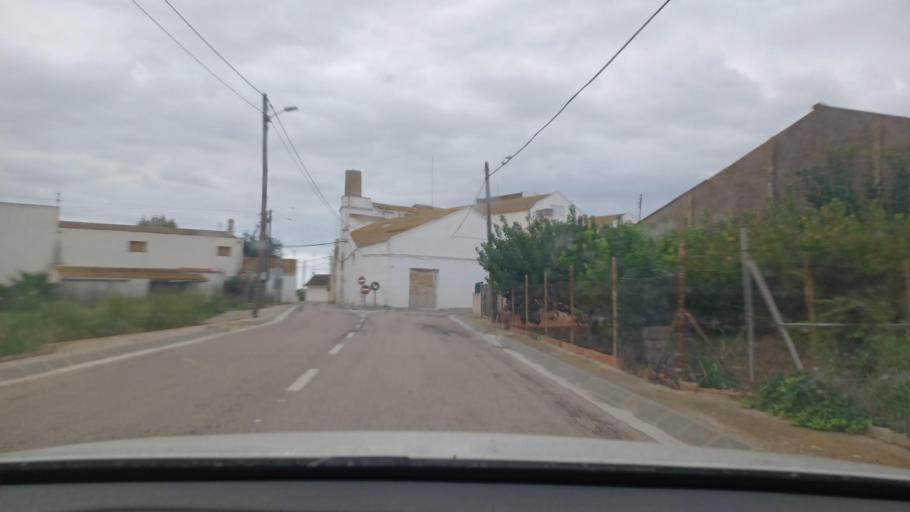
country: ES
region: Catalonia
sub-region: Provincia de Tarragona
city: Deltebre
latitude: 40.7249
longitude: 0.6810
